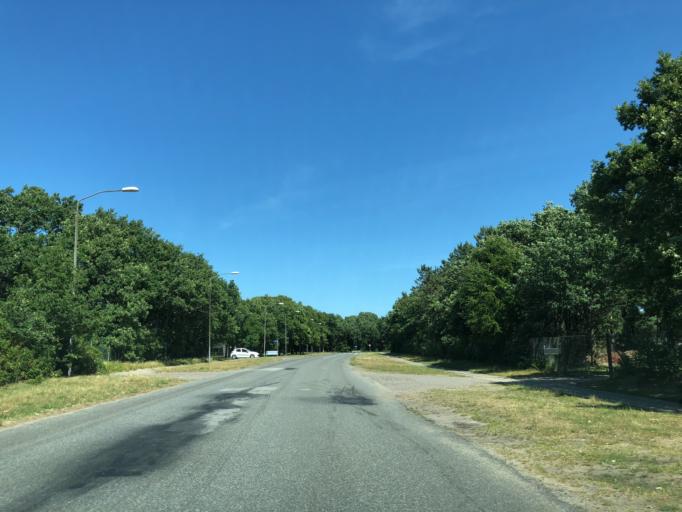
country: DK
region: Central Jutland
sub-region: Skive Kommune
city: Skive
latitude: 56.5483
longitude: 9.0230
